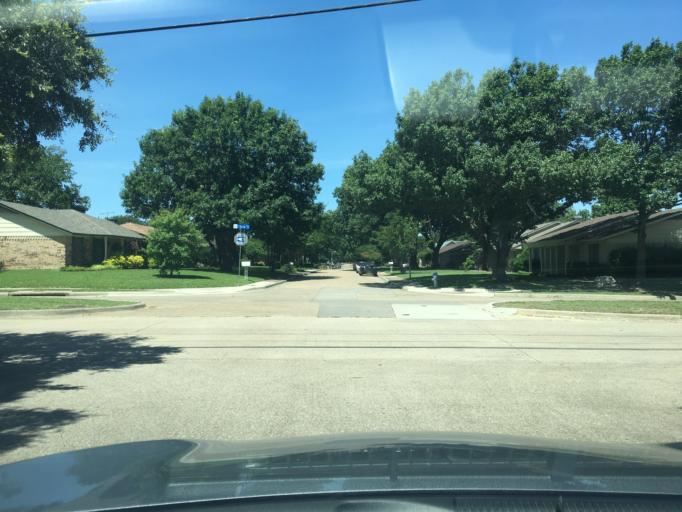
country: US
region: Texas
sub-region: Dallas County
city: Richardson
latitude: 32.9484
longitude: -96.6911
